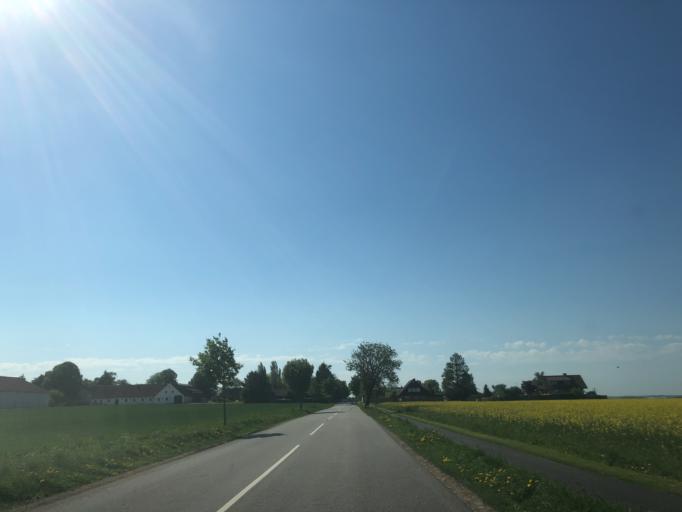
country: DK
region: Zealand
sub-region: Roskilde Kommune
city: Viby
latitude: 55.5706
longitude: 12.0736
